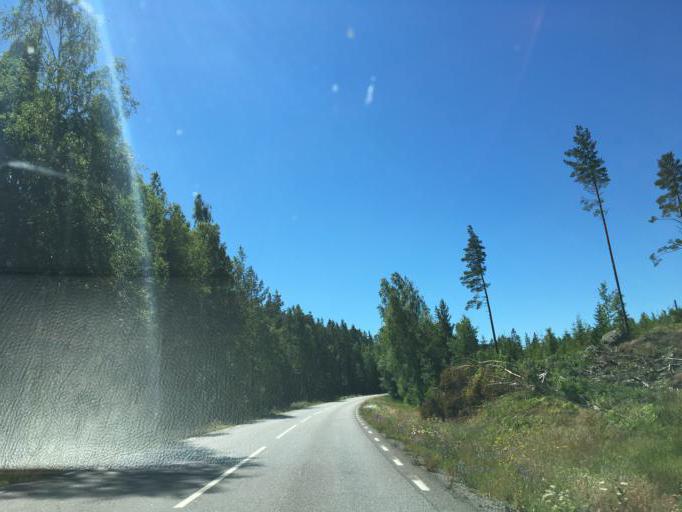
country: SE
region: OErebro
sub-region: Laxa Kommun
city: Laxa
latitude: 58.8170
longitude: 14.5506
